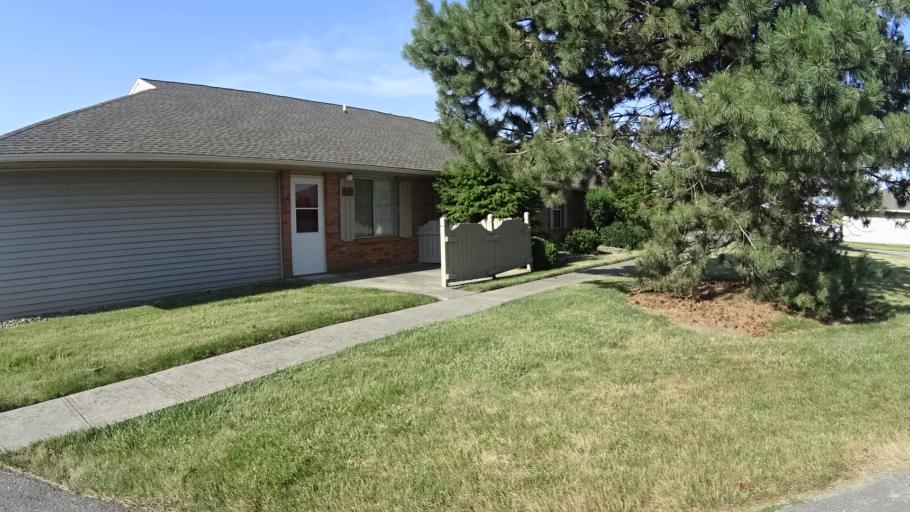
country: US
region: Ohio
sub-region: Erie County
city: Sandusky
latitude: 41.4454
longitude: -82.7820
